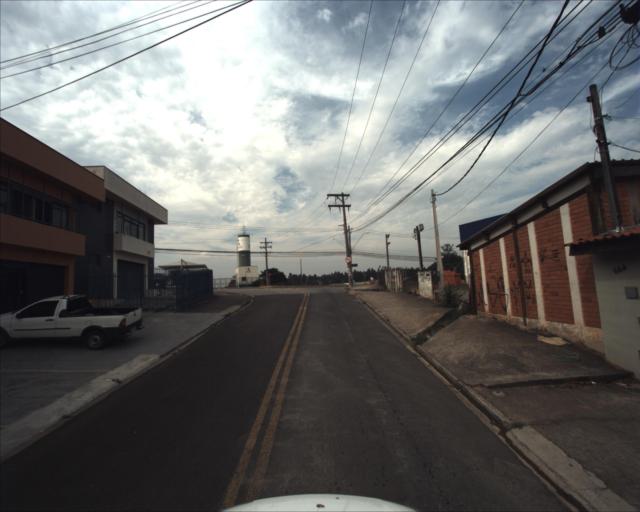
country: BR
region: Sao Paulo
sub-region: Sorocaba
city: Sorocaba
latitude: -23.4636
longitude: -47.4343
